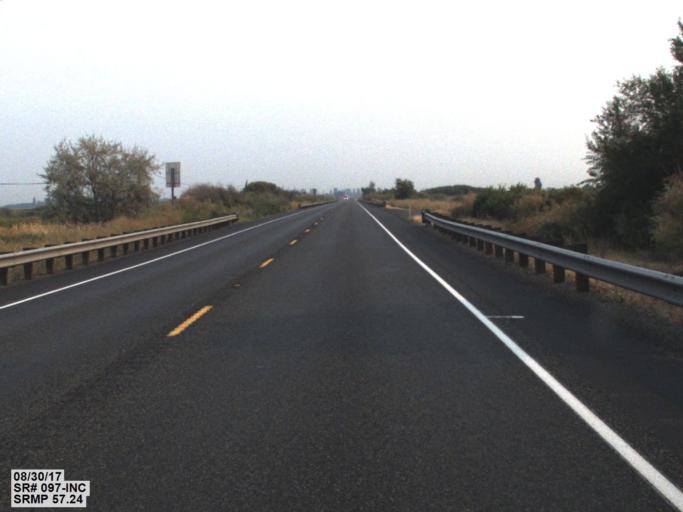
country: US
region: Washington
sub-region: Yakima County
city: Toppenish
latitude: 46.3114
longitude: -120.3299
